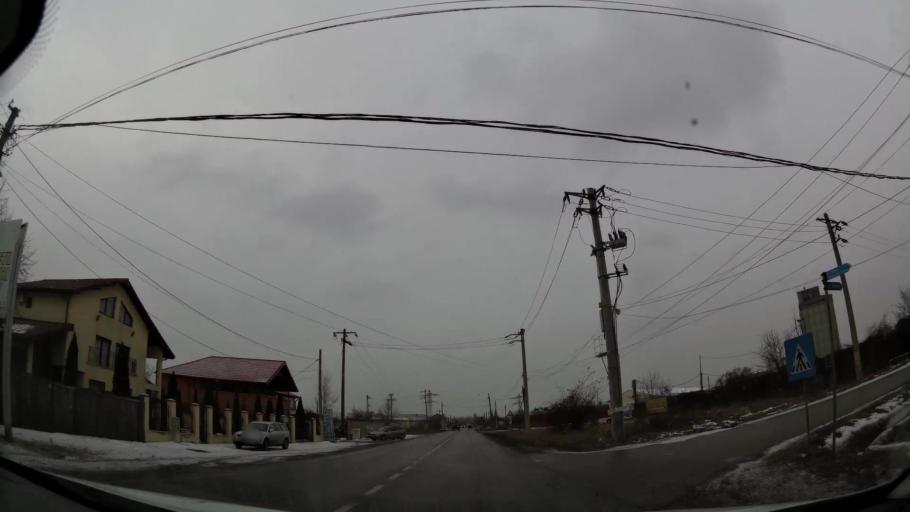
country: RO
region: Dambovita
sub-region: Comuna Aninoasa
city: Viforata
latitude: 44.9478
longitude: 25.4701
